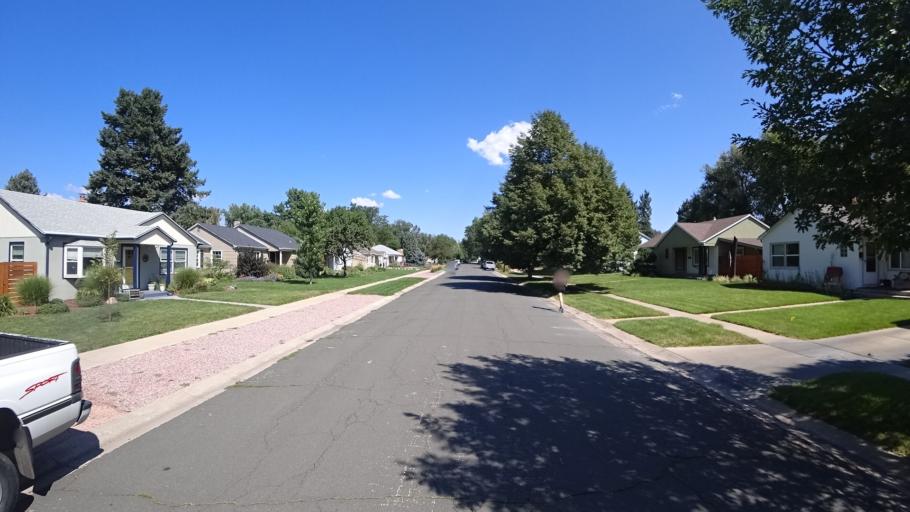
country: US
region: Colorado
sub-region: El Paso County
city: Colorado Springs
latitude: 38.8657
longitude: -104.8103
